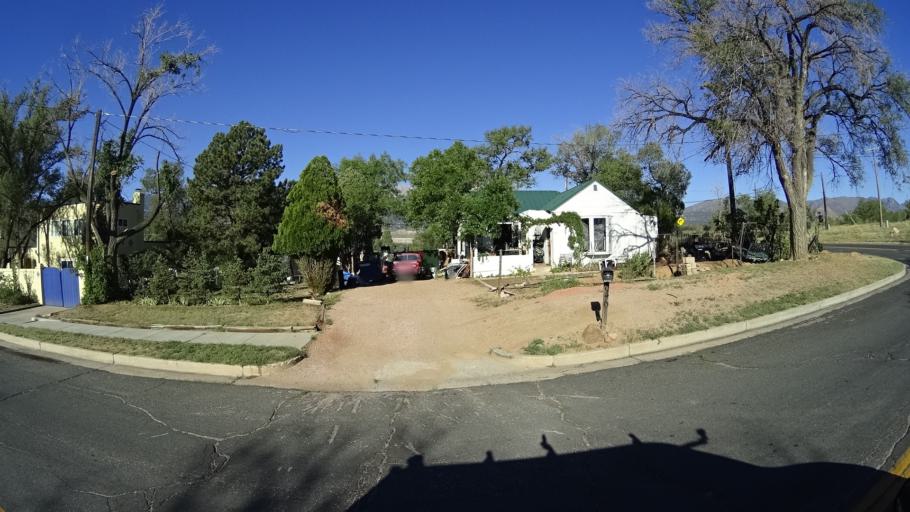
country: US
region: Colorado
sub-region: El Paso County
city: Colorado Springs
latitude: 38.8441
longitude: -104.8395
